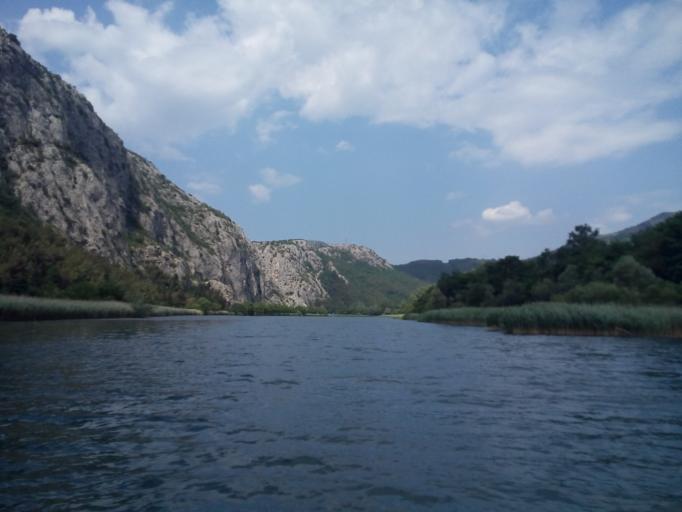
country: HR
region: Splitsko-Dalmatinska
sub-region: Grad Omis
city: Omis
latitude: 43.4501
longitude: 16.7122
